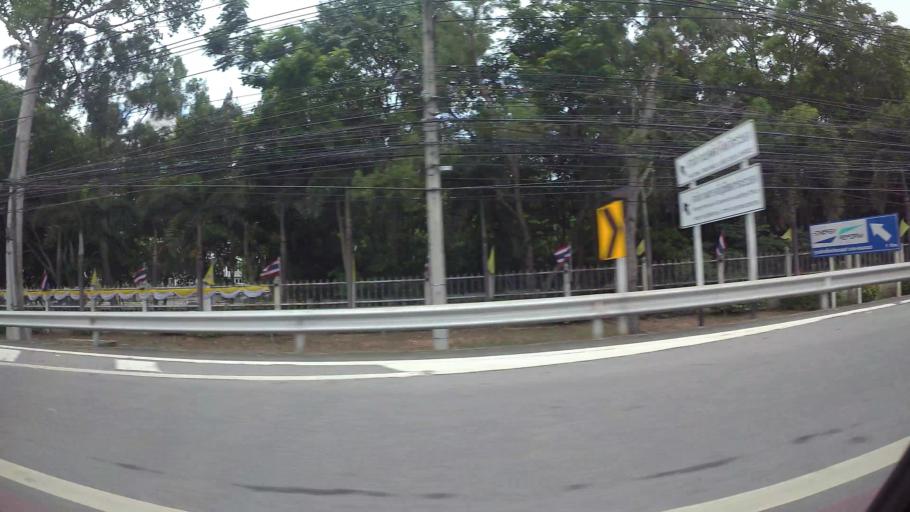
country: TH
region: Rayong
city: Rayong
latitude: 12.6836
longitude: 101.2184
